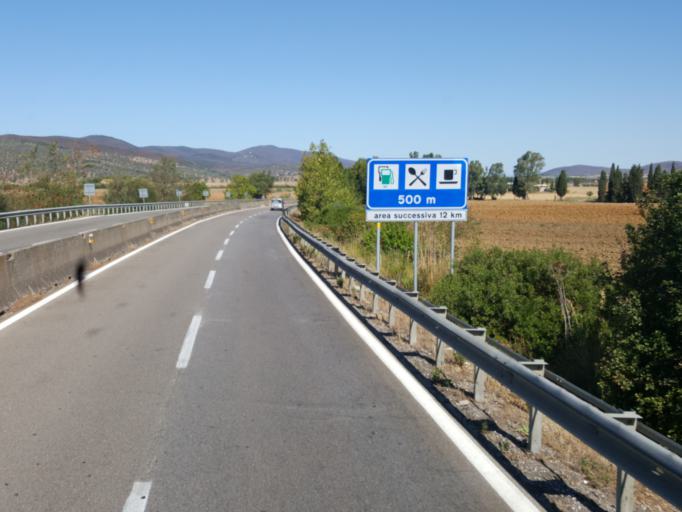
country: IT
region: Tuscany
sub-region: Provincia di Grosseto
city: Fonteblanda
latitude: 42.5691
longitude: 11.1698
